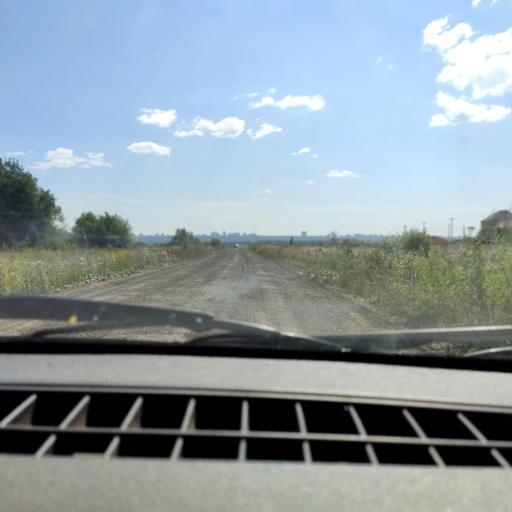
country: RU
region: Bashkortostan
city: Mikhaylovka
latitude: 54.8121
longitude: 55.9460
